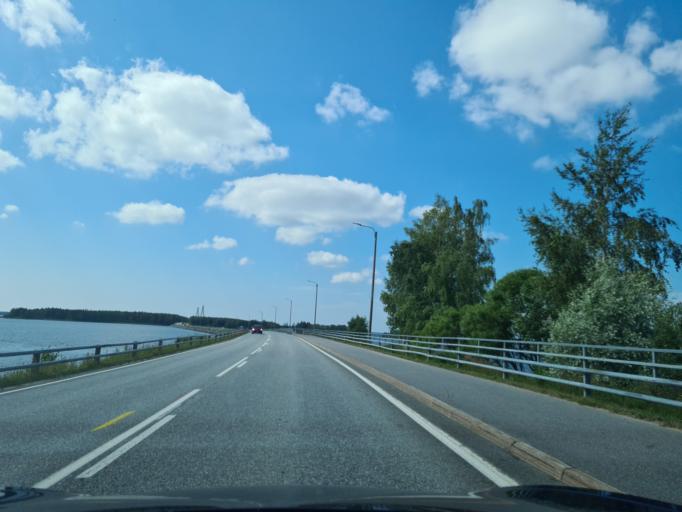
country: FI
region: Ostrobothnia
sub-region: Vaasa
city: Replot
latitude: 63.2050
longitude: 21.5190
